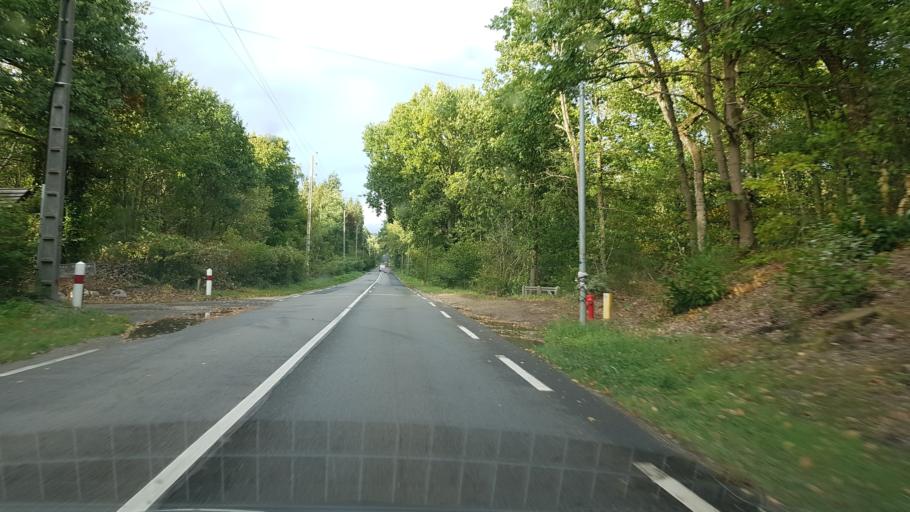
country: FR
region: Ile-de-France
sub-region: Departement de l'Essonne
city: Fontenay-les-Briis
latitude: 48.6203
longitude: 2.1712
